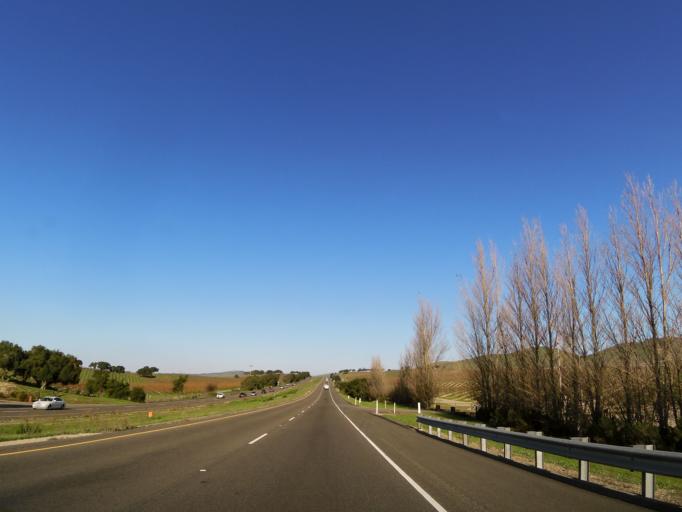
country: US
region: California
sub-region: Santa Barbara County
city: Los Alamos
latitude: 34.7706
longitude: -120.3069
